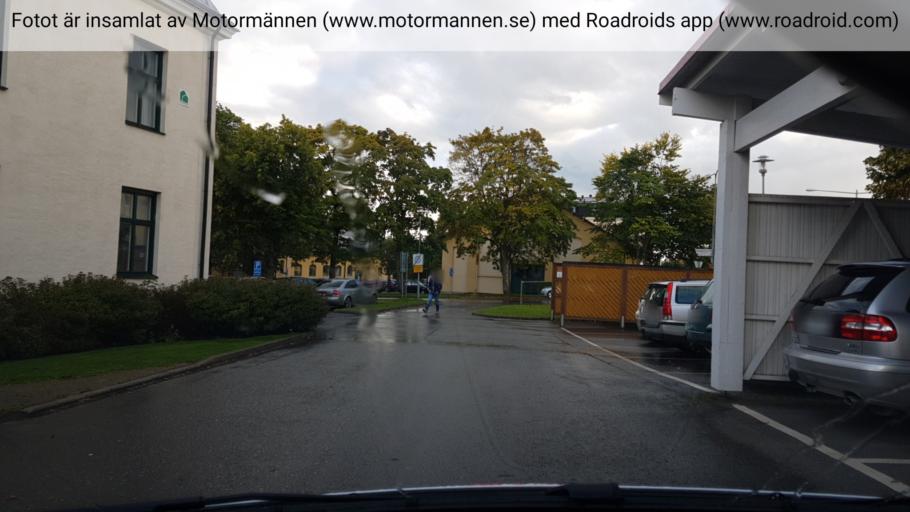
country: SE
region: Vaestra Goetaland
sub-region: Skovde Kommun
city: Skoevde
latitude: 58.3965
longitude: 13.8548
